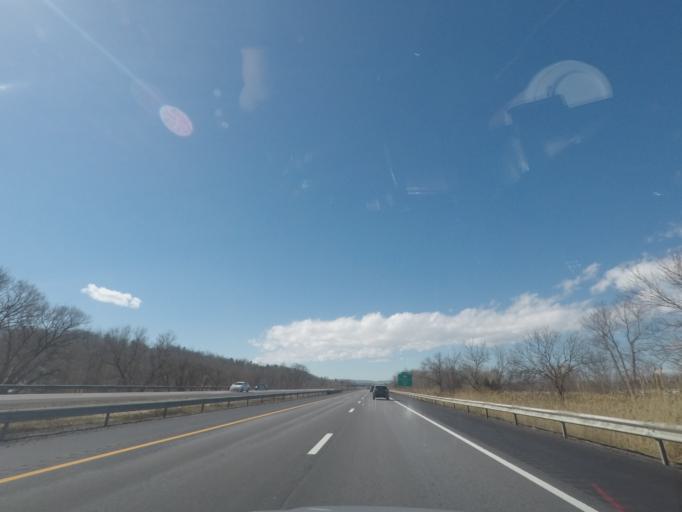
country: US
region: New York
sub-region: Montgomery County
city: Fonda
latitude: 42.9433
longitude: -74.3515
